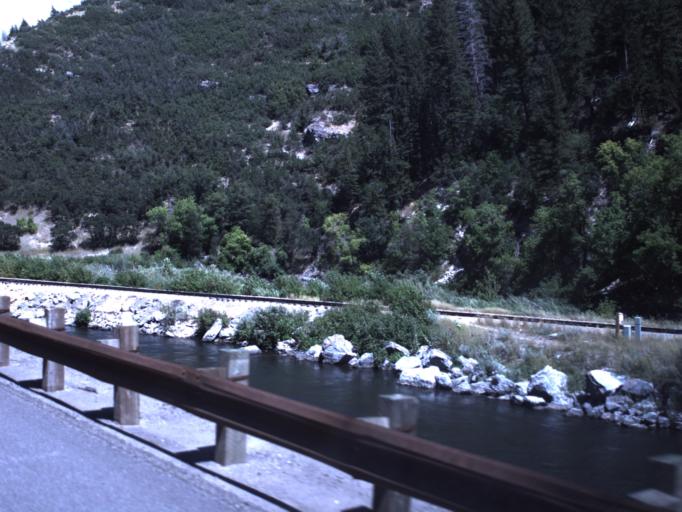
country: US
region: Utah
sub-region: Utah County
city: Orem
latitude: 40.3725
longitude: -111.5555
